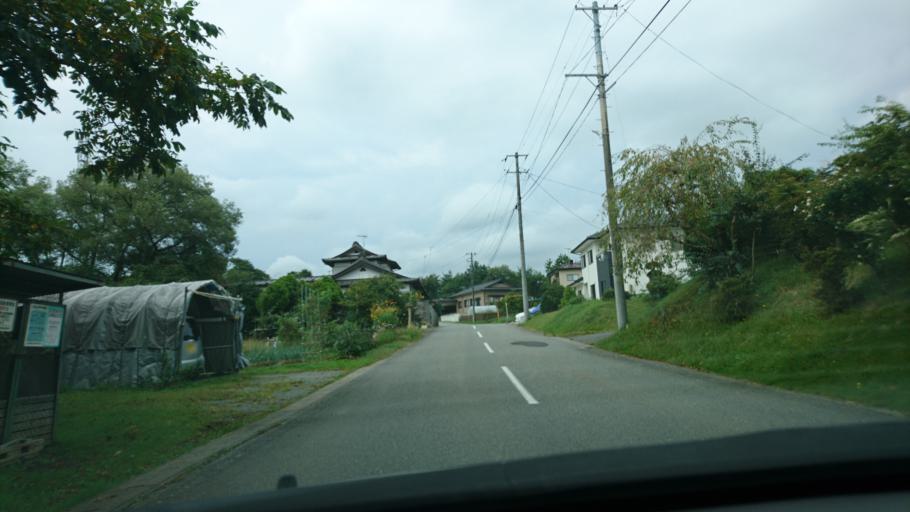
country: JP
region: Miyagi
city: Furukawa
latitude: 38.7205
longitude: 141.0323
